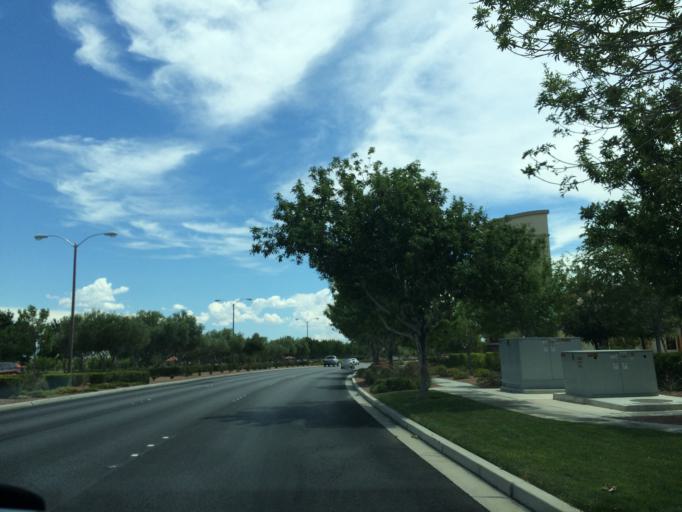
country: US
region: Nevada
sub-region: Clark County
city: North Las Vegas
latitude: 36.2874
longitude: -115.1778
